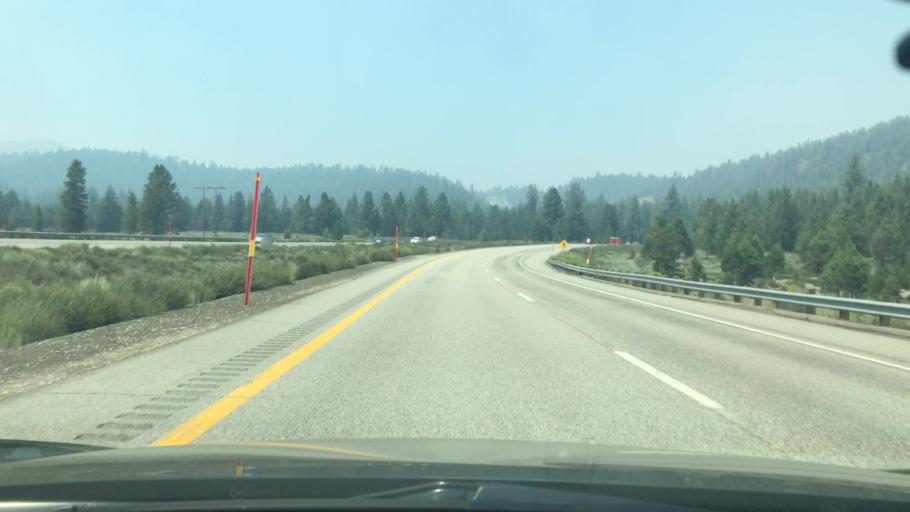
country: US
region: California
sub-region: Mono County
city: Mammoth Lakes
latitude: 37.7479
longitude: -118.9813
